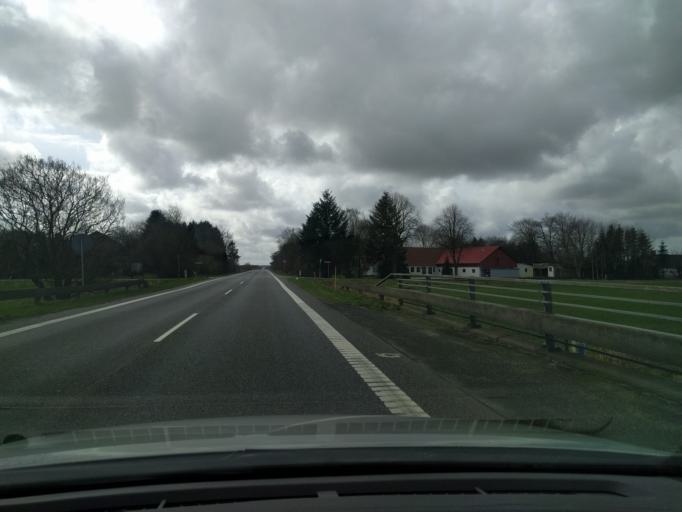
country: DK
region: South Denmark
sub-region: Tonder Kommune
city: Toftlund
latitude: 55.2339
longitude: 9.1255
